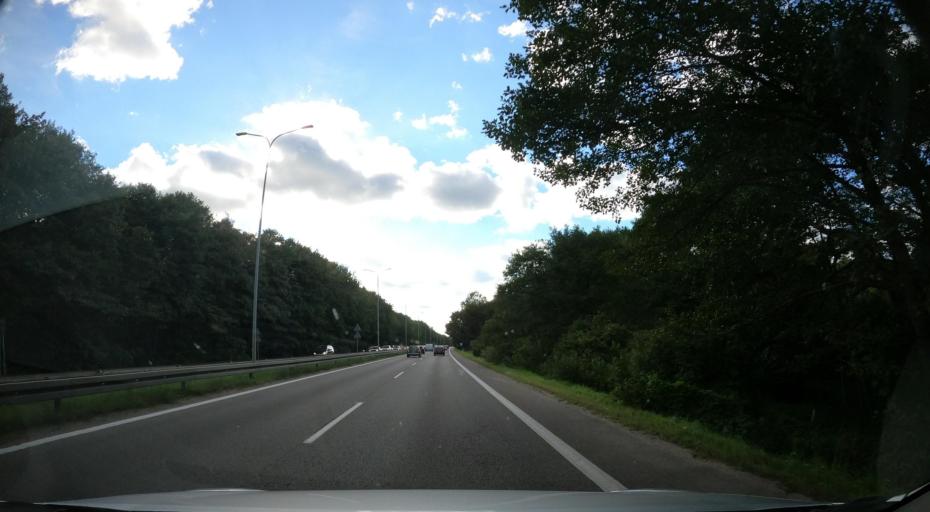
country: PL
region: Pomeranian Voivodeship
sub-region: Powiat wejherowski
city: Reda
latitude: 54.6049
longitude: 18.3360
